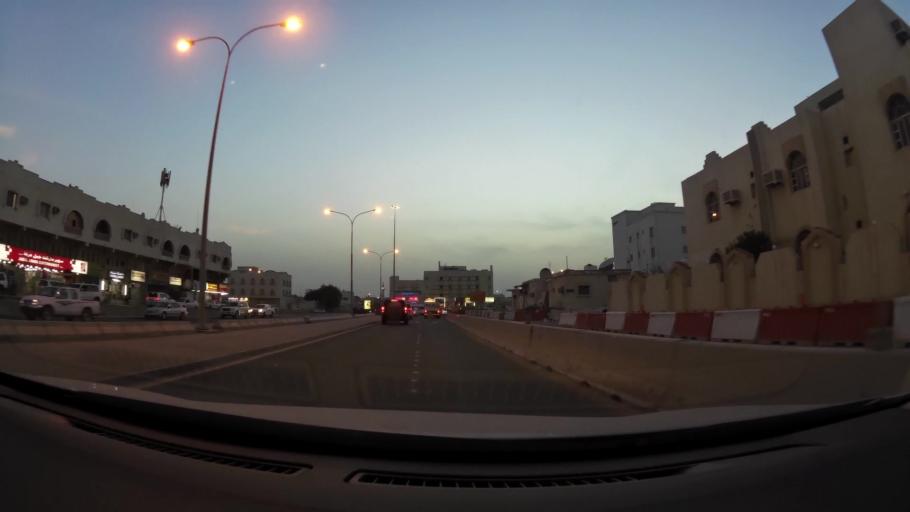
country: QA
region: Al Wakrah
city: Al Wakrah
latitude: 25.1615
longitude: 51.5999
